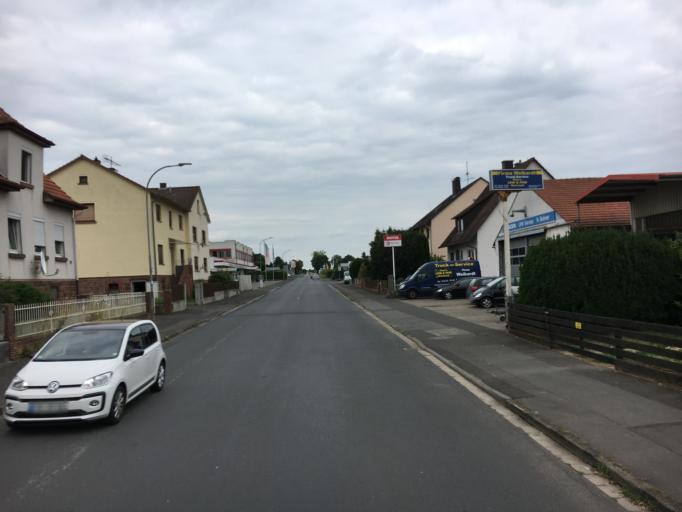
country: DE
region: Hesse
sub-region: Regierungsbezirk Giessen
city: Kirchhain
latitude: 50.8252
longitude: 8.9364
